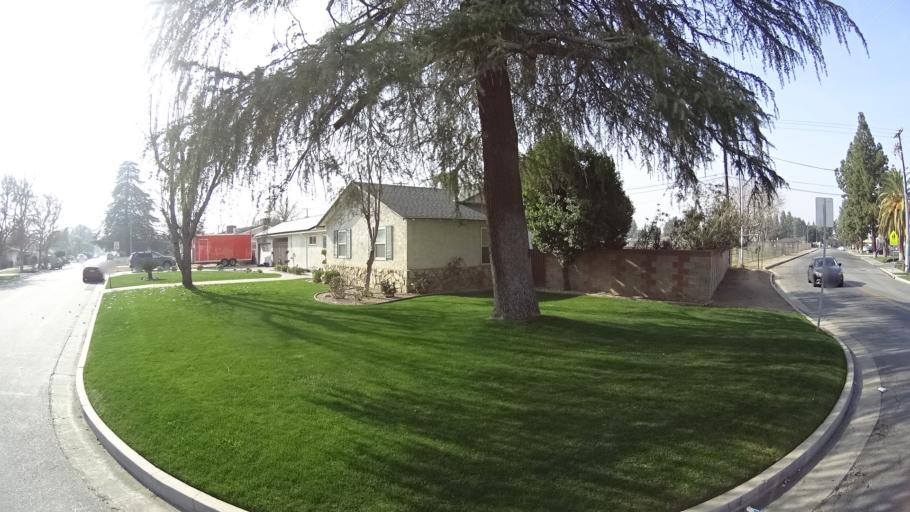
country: US
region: California
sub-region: Kern County
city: Bakersfield
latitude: 35.3652
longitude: -119.0453
